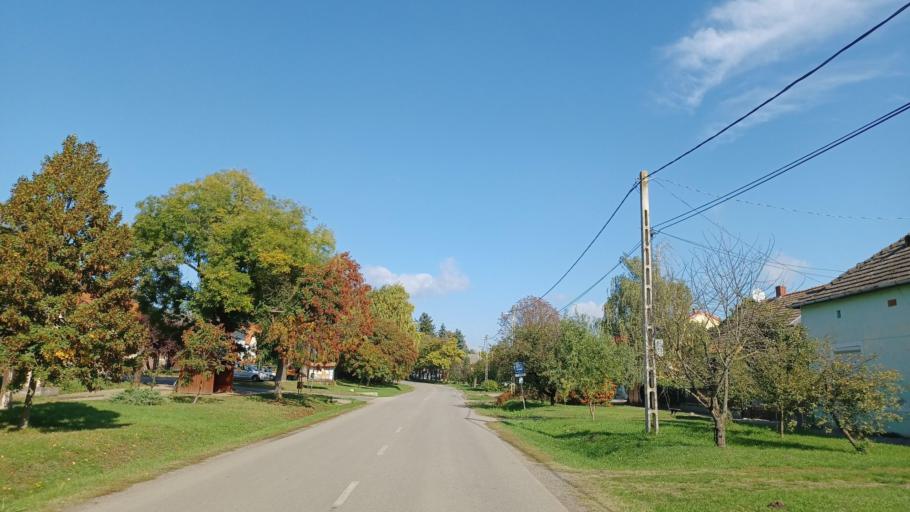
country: HU
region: Tolna
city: Nagydorog
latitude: 46.6241
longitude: 18.6068
